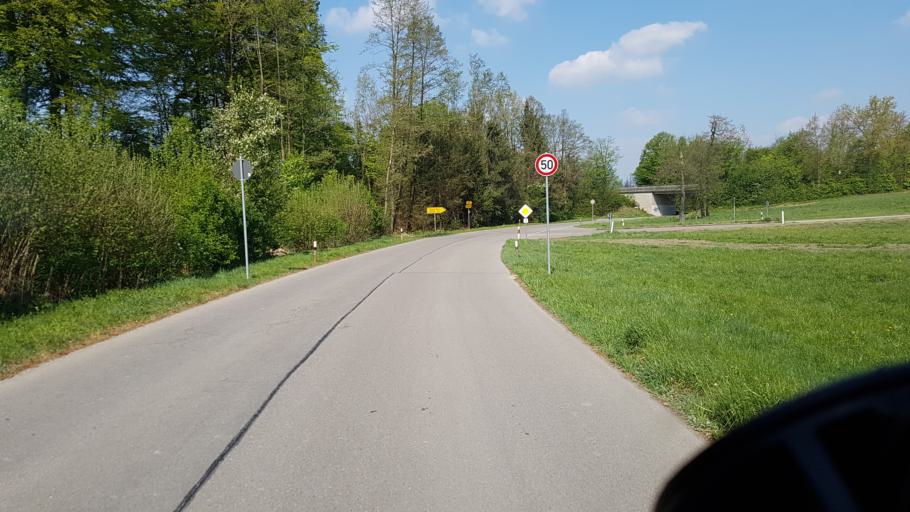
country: DE
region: Bavaria
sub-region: Upper Bavaria
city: Perach
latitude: 48.2423
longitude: 12.7411
